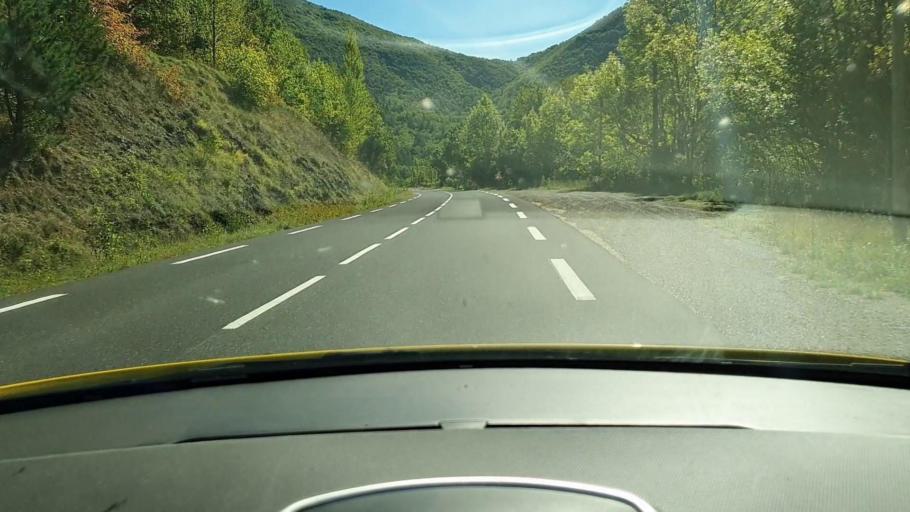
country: FR
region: Languedoc-Roussillon
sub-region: Departement du Gard
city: Le Vigan
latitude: 43.9798
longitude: 3.4694
